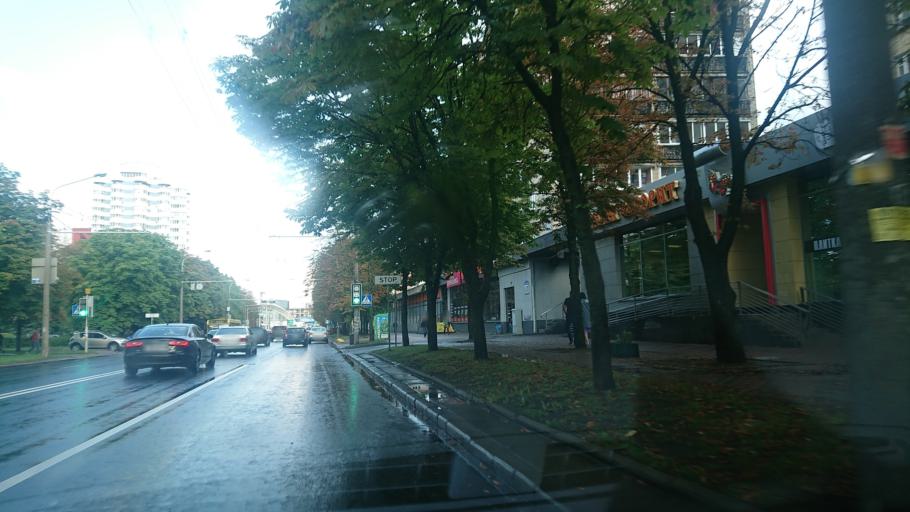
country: BY
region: Minsk
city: Minsk
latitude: 53.9205
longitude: 27.5709
